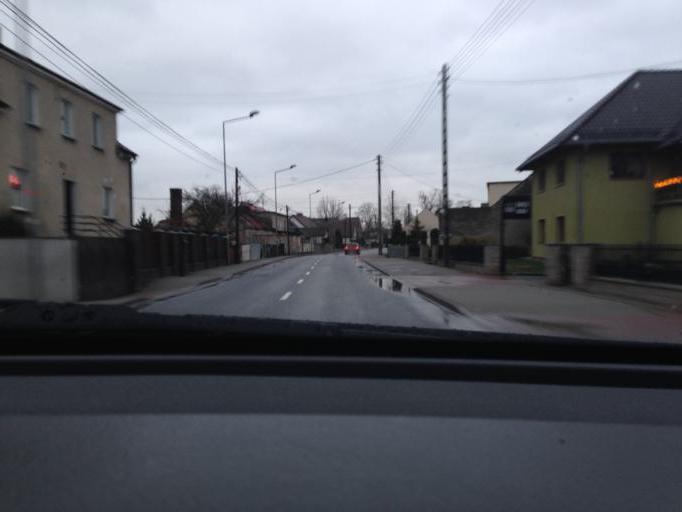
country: PL
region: Opole Voivodeship
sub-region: Powiat opolski
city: Opole
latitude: 50.6896
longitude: 17.9509
